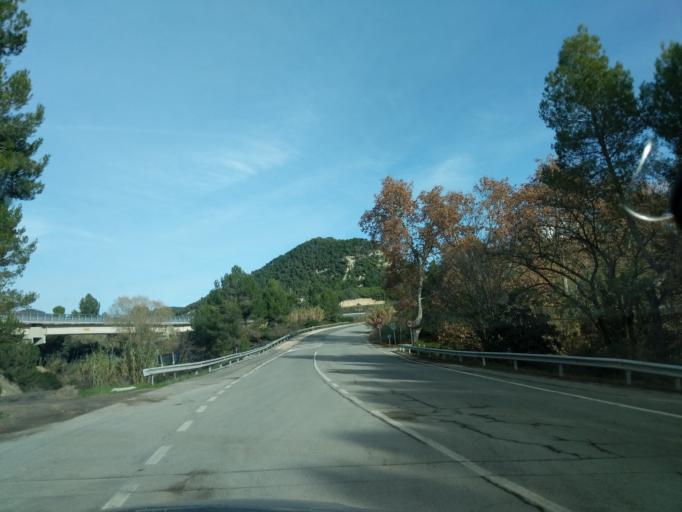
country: ES
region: Catalonia
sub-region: Provincia de Barcelona
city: Castelloli
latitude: 41.5943
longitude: 1.6825
